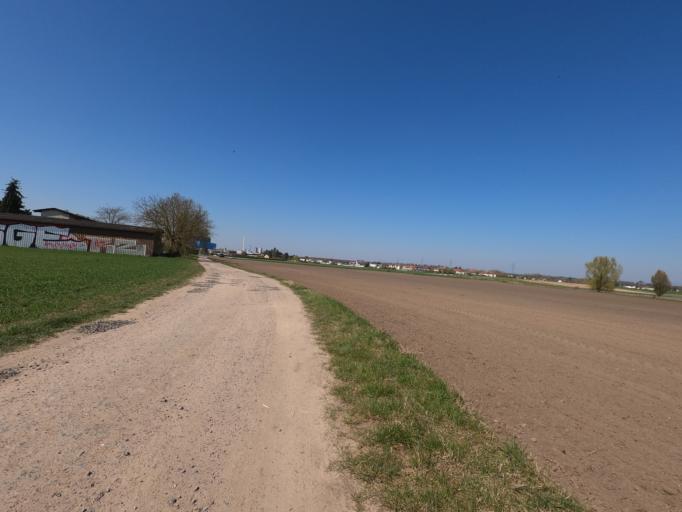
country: DE
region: Hesse
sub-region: Regierungsbezirk Darmstadt
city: Gross-Gerau
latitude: 49.9281
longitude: 8.5031
